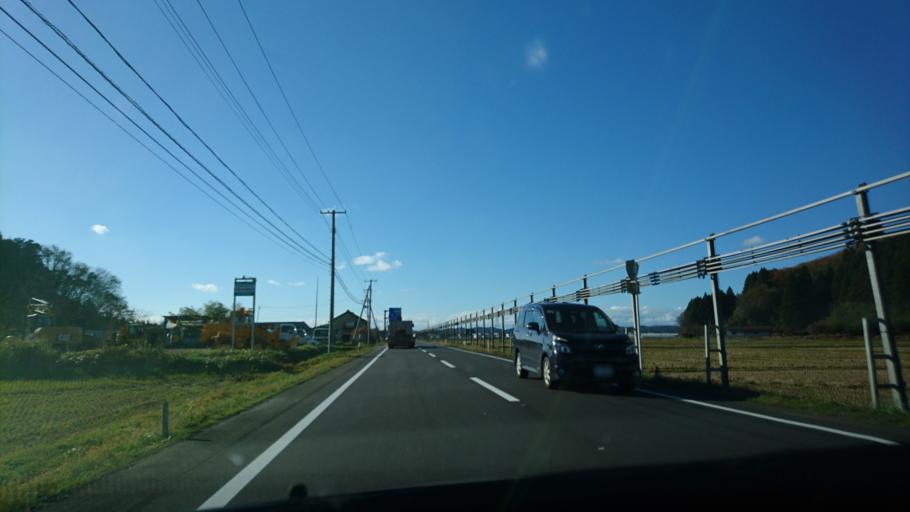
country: JP
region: Akita
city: Akita
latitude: 39.3545
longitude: 140.0873
